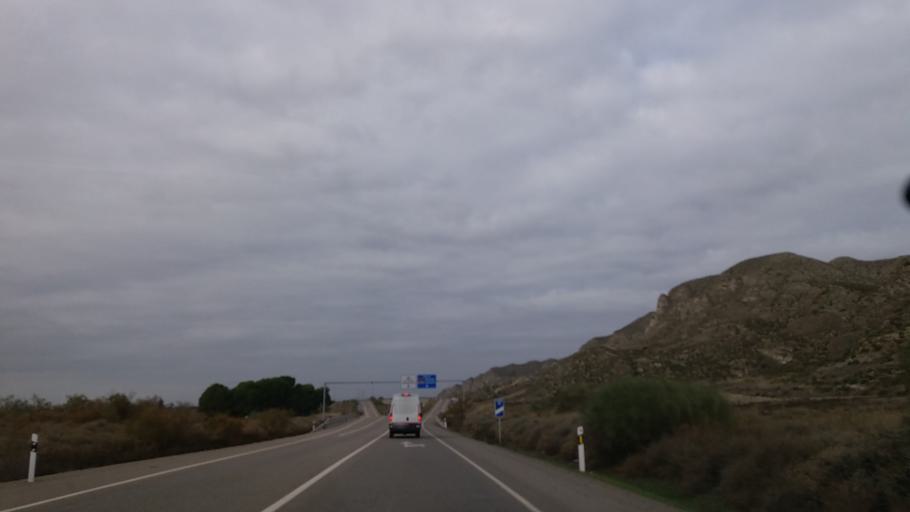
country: ES
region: Aragon
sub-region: Provincia de Zaragoza
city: Villafranca de Ebro
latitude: 41.5799
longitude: -0.6515
